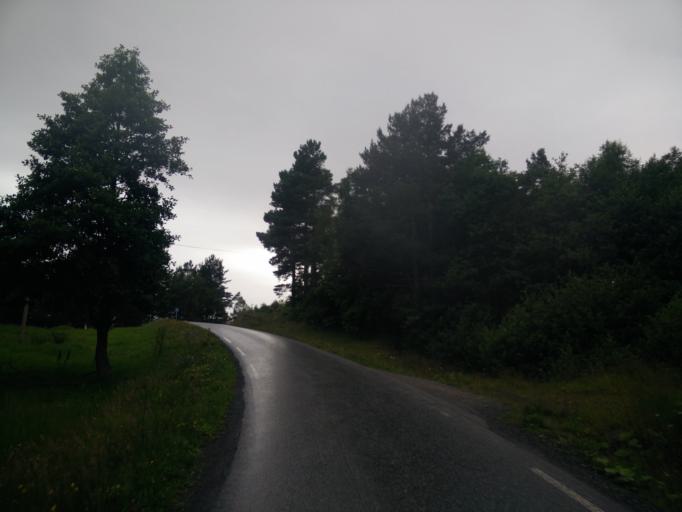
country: NO
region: More og Romsdal
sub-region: Kristiansund
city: Rensvik
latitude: 63.0187
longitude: 7.9018
